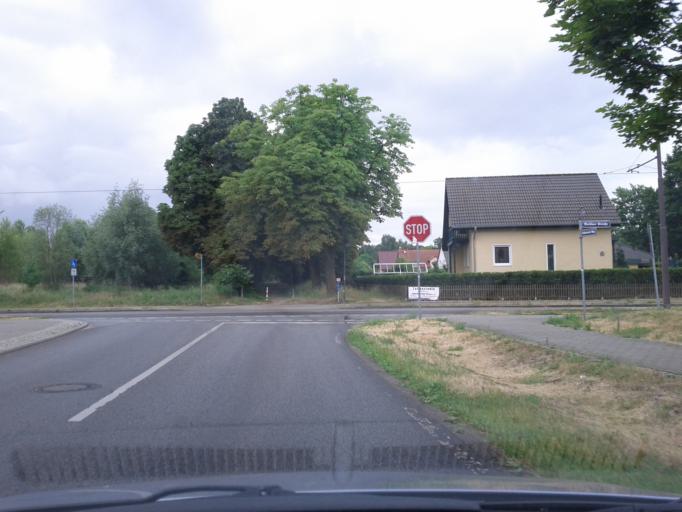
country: DE
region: Brandenburg
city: Woltersdorf
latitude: 52.4547
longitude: 13.7378
